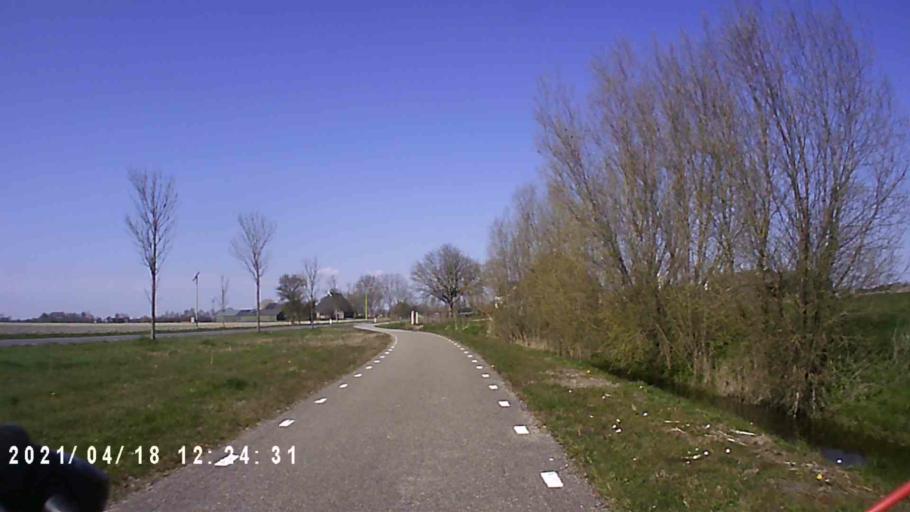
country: NL
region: Friesland
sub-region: Gemeente Dongeradeel
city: Anjum
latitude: 53.3276
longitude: 6.1172
